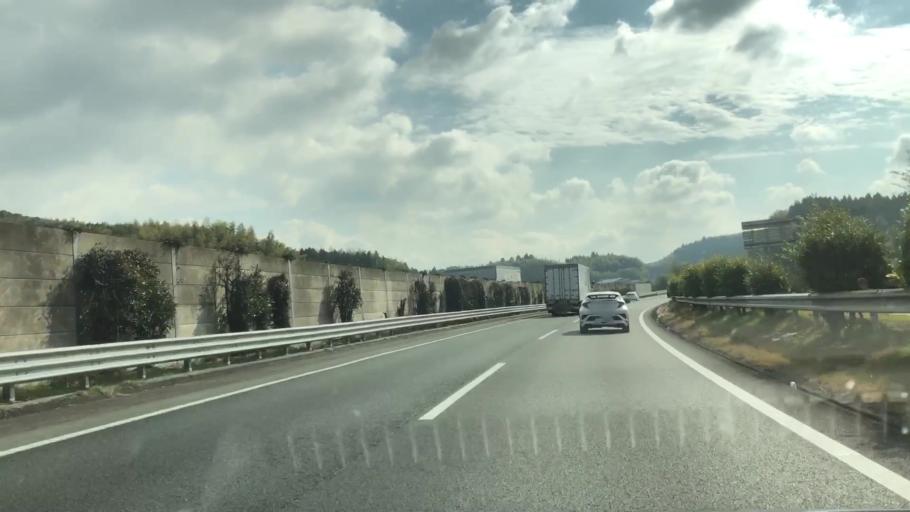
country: JP
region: Fukuoka
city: Setakamachi-takayanagi
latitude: 33.0847
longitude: 130.5416
